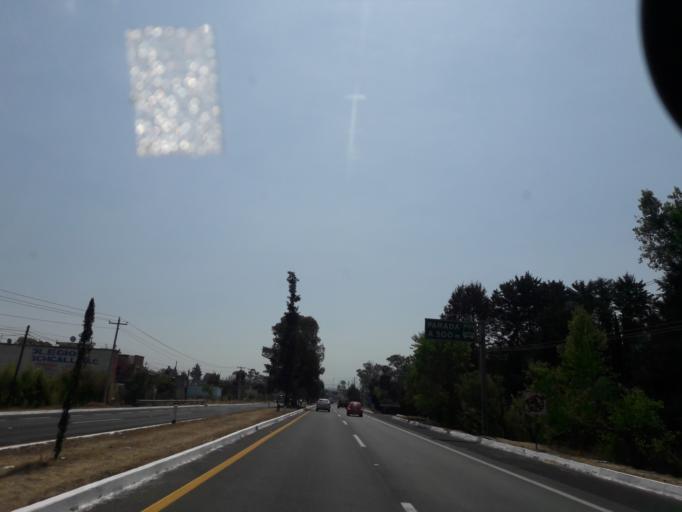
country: MX
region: Tlaxcala
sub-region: Totolac
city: Zaragoza
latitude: 19.3214
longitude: -98.2682
